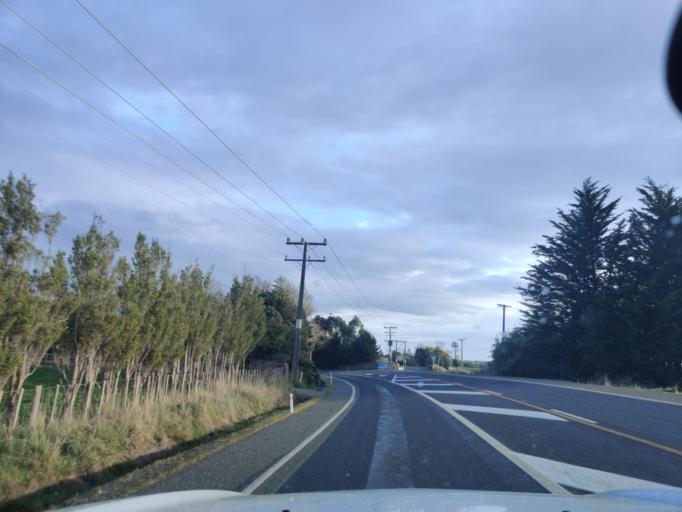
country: NZ
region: Manawatu-Wanganui
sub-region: Palmerston North City
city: Palmerston North
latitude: -40.3994
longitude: 175.6220
